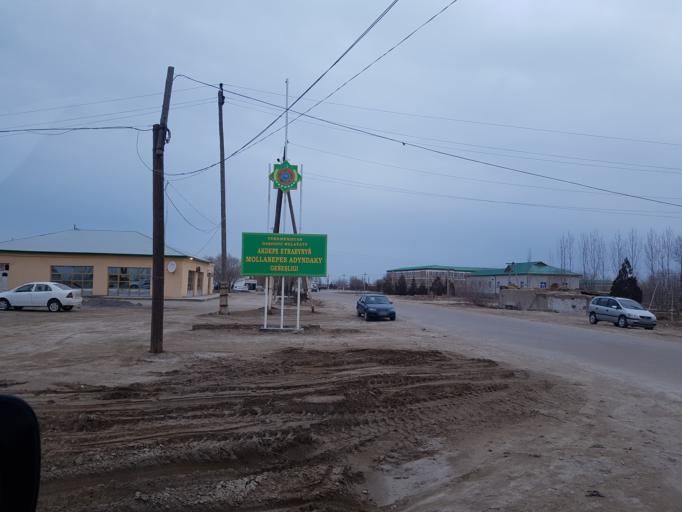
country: TM
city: Akdepe
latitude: 41.9788
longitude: 59.4739
